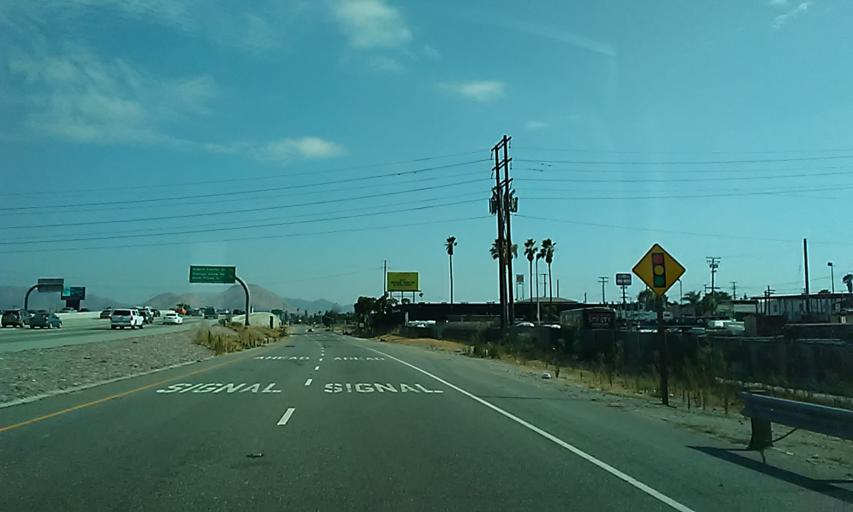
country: US
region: California
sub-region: San Bernardino County
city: San Bernardino
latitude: 34.0946
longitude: -117.3023
